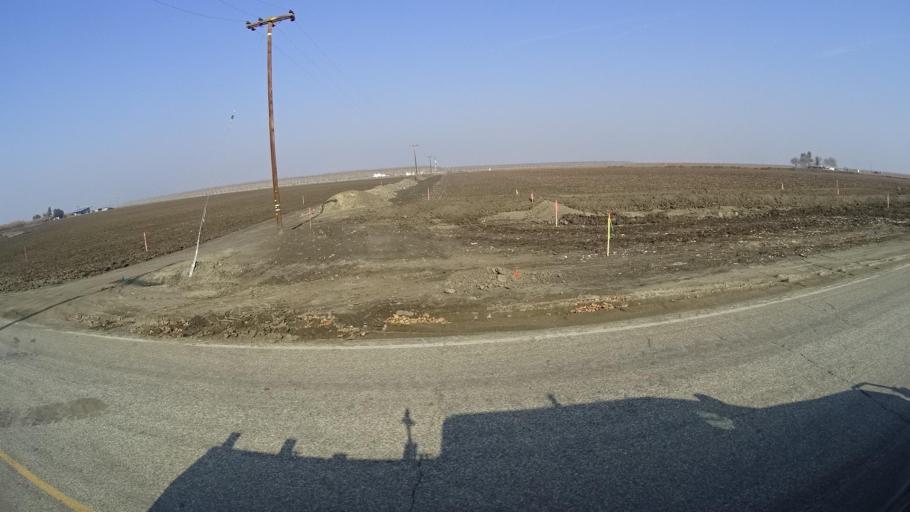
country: US
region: California
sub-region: Kern County
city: Buttonwillow
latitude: 35.3546
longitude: -119.4166
